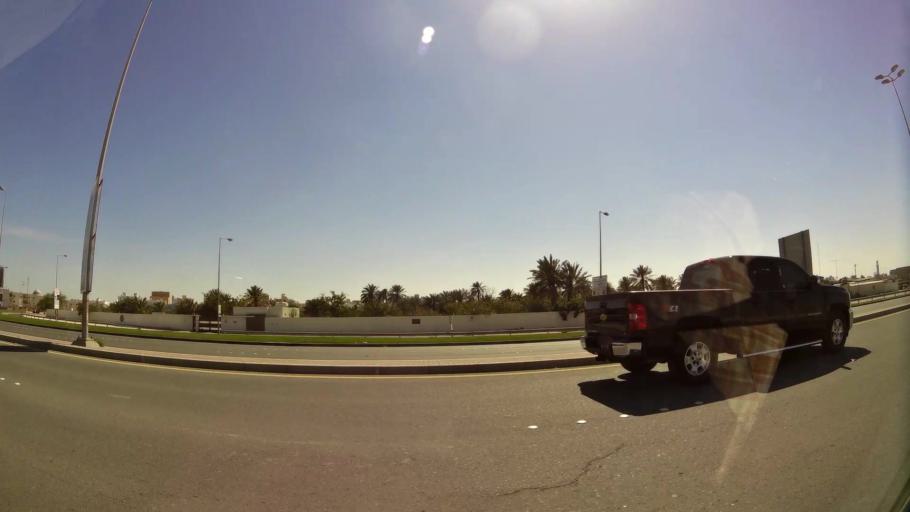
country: BH
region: Muharraq
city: Al Hadd
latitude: 26.2560
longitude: 50.6524
